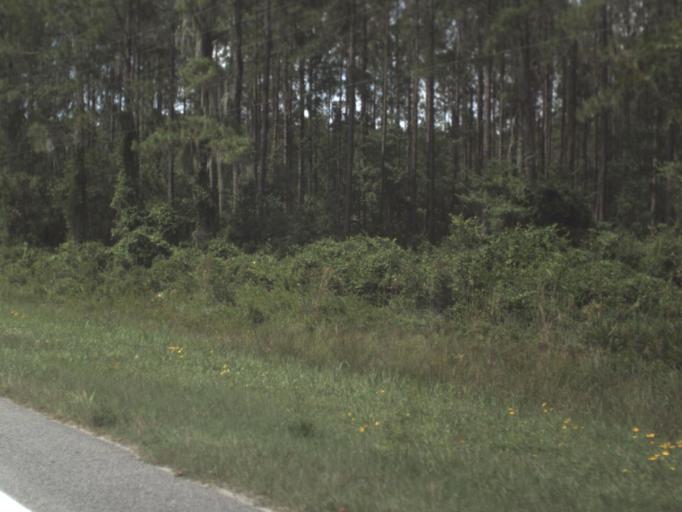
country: US
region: Florida
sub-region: Hamilton County
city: Jasper
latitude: 30.4403
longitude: -82.9339
